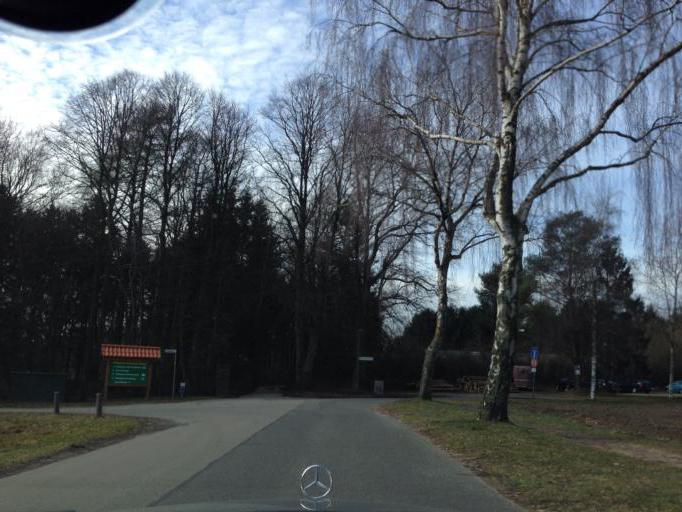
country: DE
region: Lower Saxony
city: Seevetal
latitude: 53.4432
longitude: 9.8914
